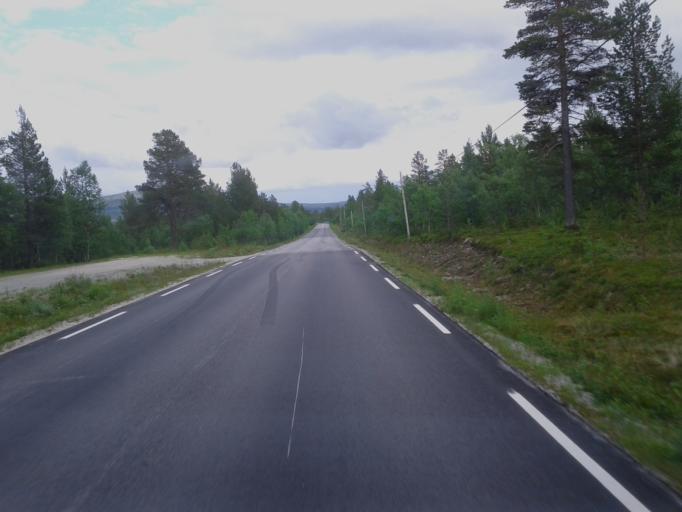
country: NO
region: Sor-Trondelag
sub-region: Roros
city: Roros
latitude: 62.3114
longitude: 11.6712
